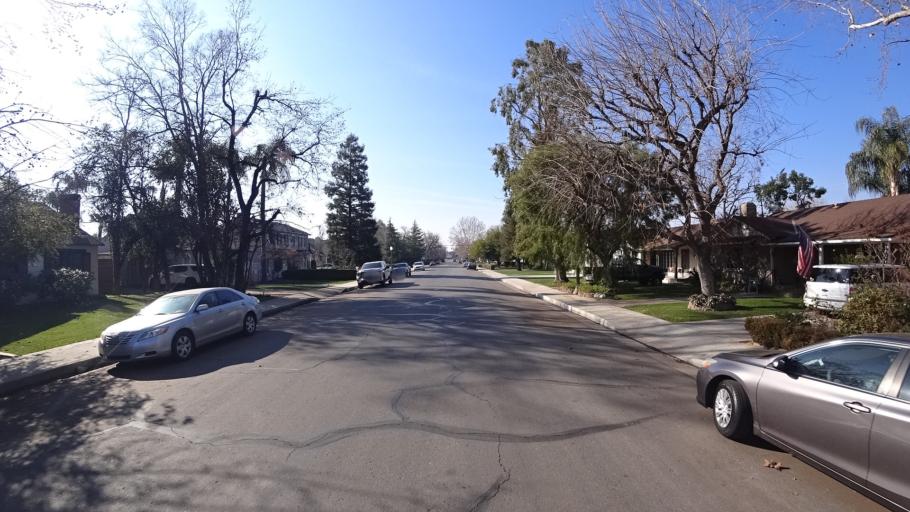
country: US
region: California
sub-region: Kern County
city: Bakersfield
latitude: 35.3667
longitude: -119.0330
